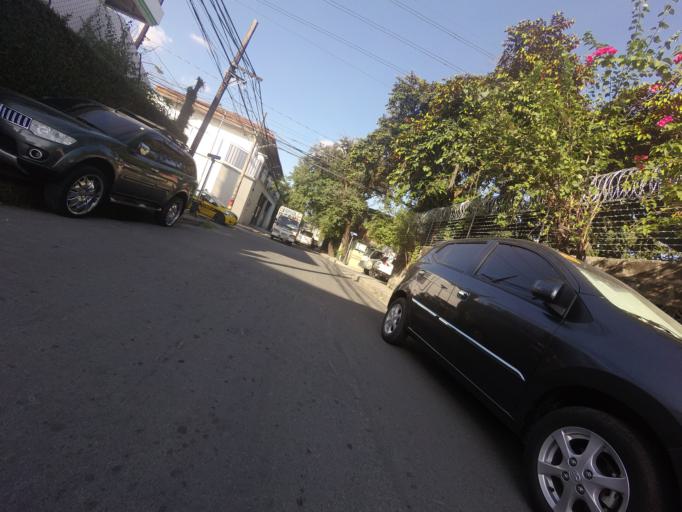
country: PH
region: Metro Manila
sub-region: San Juan
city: San Juan
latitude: 14.5916
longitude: 121.0346
